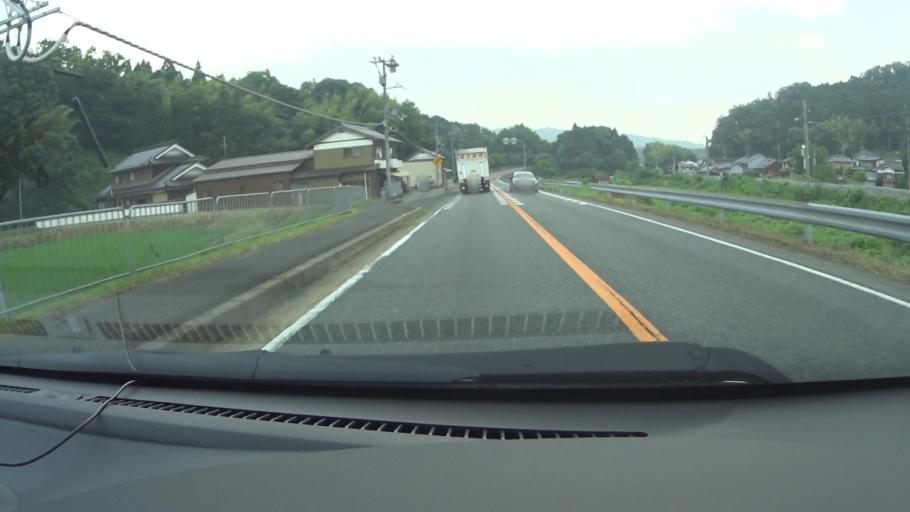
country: JP
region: Kyoto
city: Ayabe
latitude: 35.3448
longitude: 135.3116
